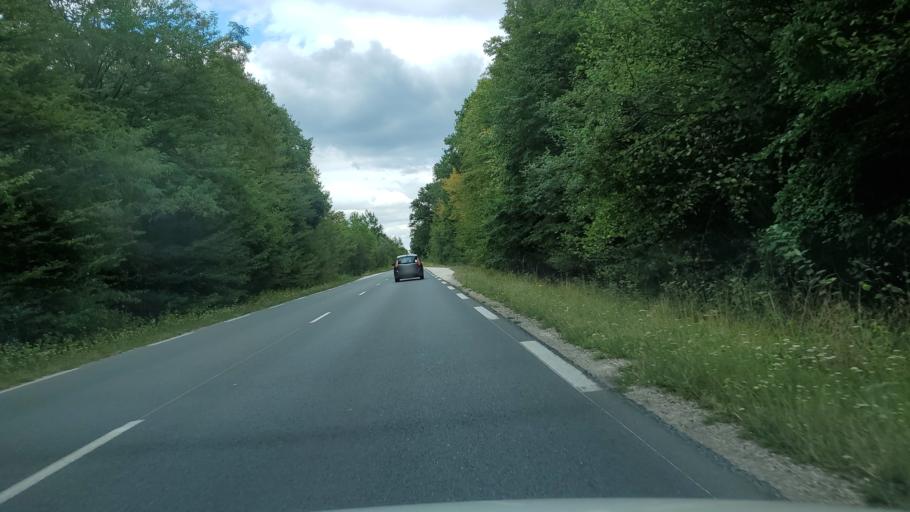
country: FR
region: Ile-de-France
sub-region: Departement de Seine-et-Marne
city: La Houssaye-en-Brie
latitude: 48.7857
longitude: 2.8806
